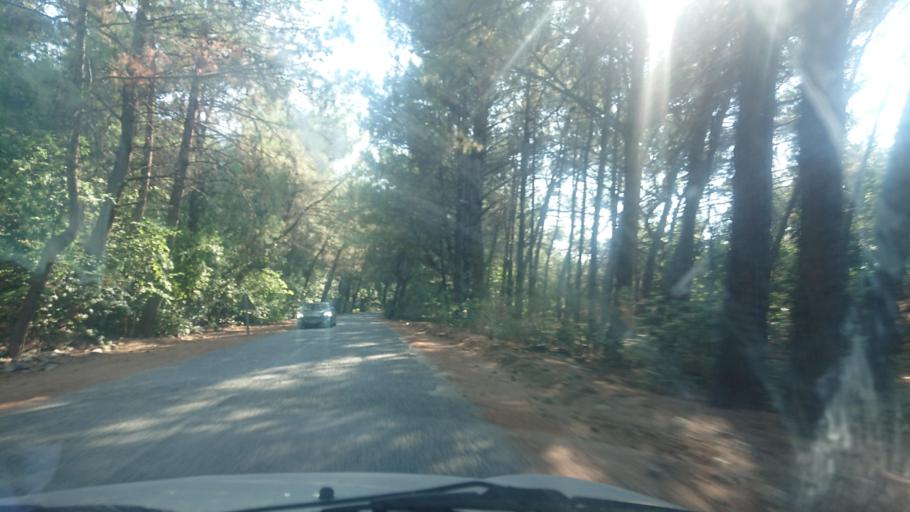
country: TR
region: Aydin
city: Atburgazi
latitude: 37.6905
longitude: 27.1402
